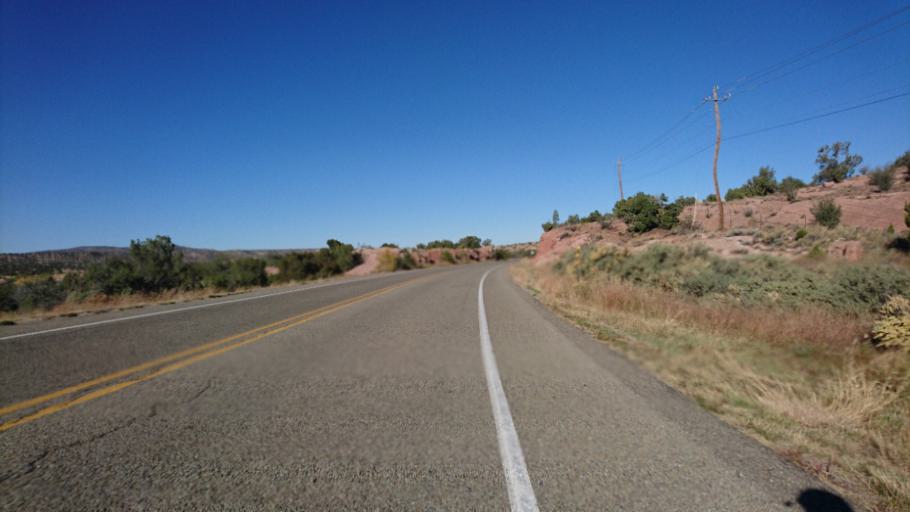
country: US
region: New Mexico
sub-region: Santa Fe County
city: La Cienega
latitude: 35.4297
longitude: -106.0939
